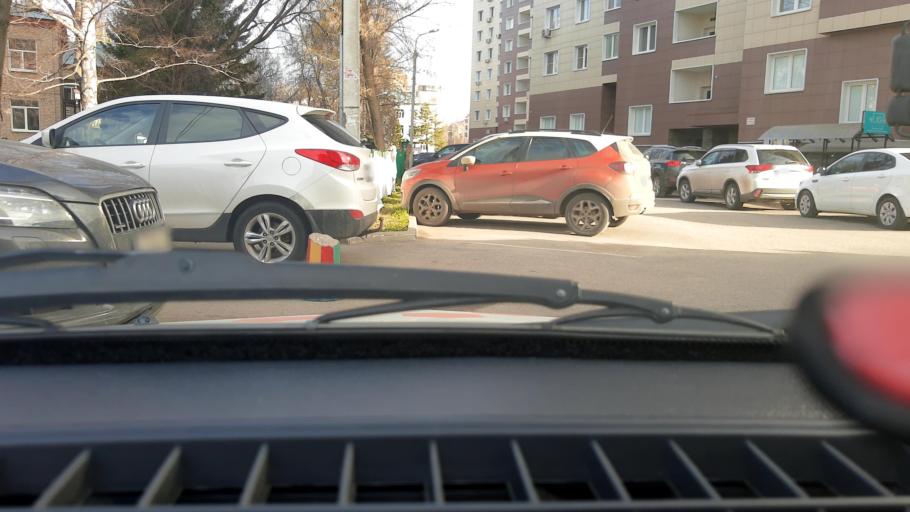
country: RU
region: Bashkortostan
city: Ufa
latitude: 54.7560
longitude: 56.0093
